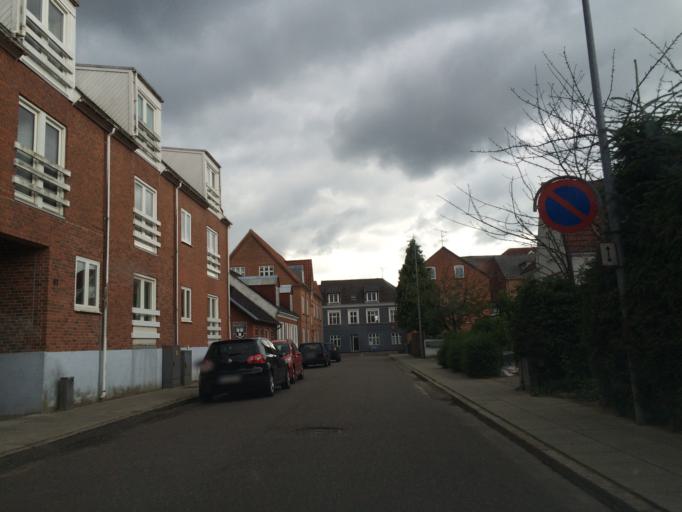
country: DK
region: Central Jutland
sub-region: Silkeborg Kommune
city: Silkeborg
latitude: 56.1652
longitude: 9.5387
